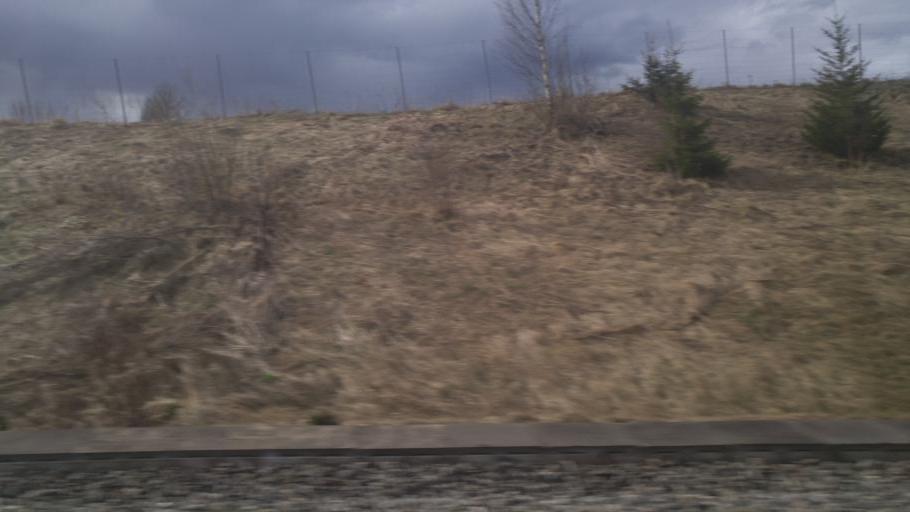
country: NO
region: Akershus
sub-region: Skedsmo
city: Leirsund
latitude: 60.0029
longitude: 11.0911
